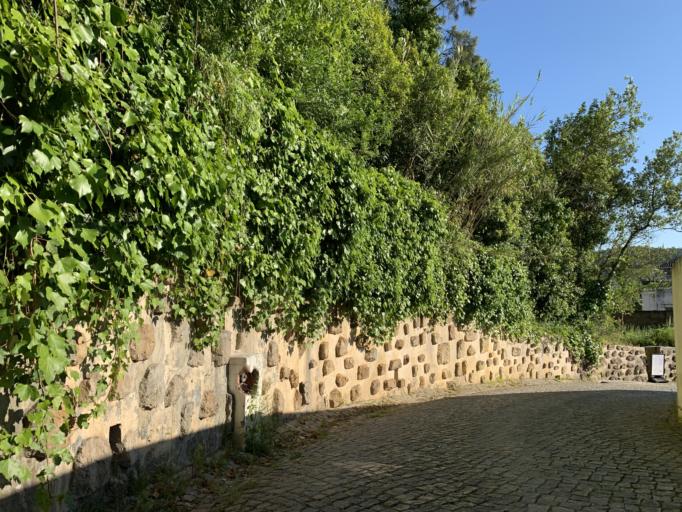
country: PT
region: Coimbra
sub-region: Coimbra
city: Coimbra
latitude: 40.2041
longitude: -8.4241
